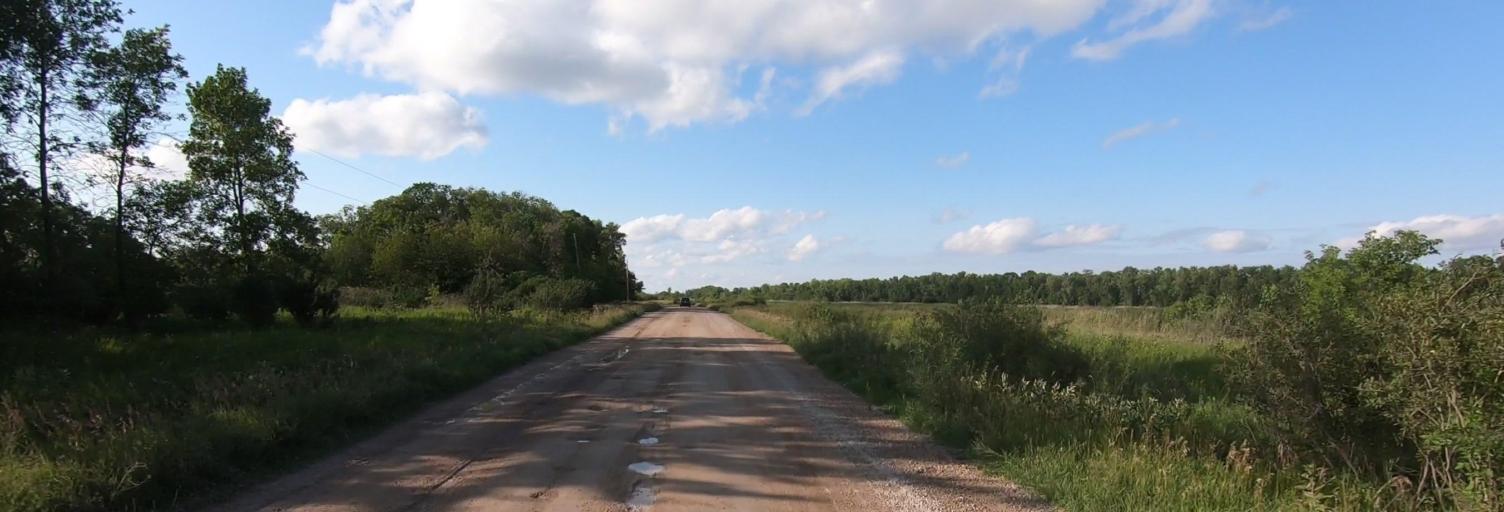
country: CA
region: Manitoba
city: Selkirk
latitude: 50.2454
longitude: -96.8446
